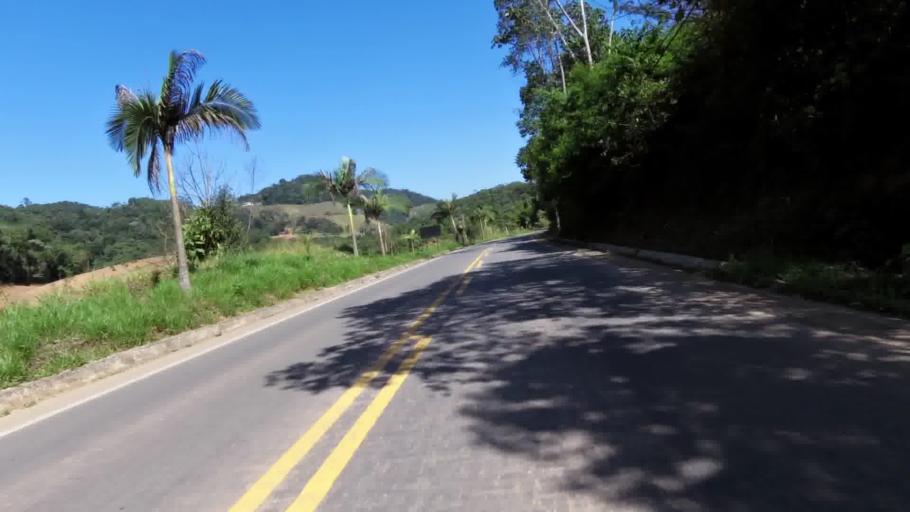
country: BR
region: Espirito Santo
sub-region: Marechal Floriano
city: Marechal Floriano
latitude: -20.4828
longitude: -40.7704
